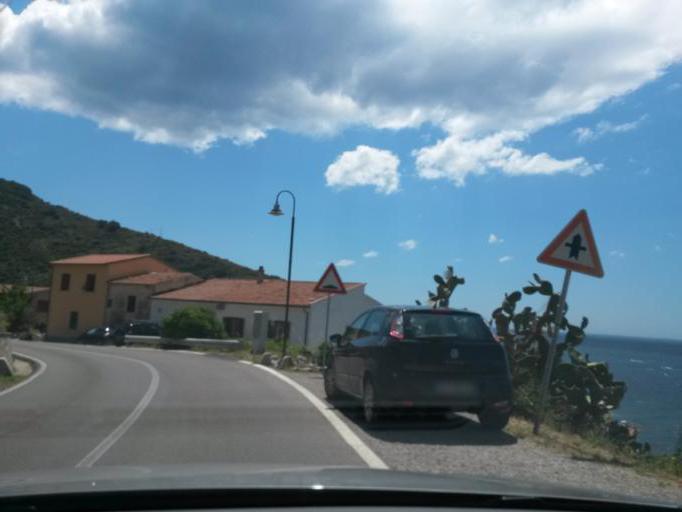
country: IT
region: Tuscany
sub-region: Provincia di Livorno
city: Marciana
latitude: 42.7499
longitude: 10.1189
